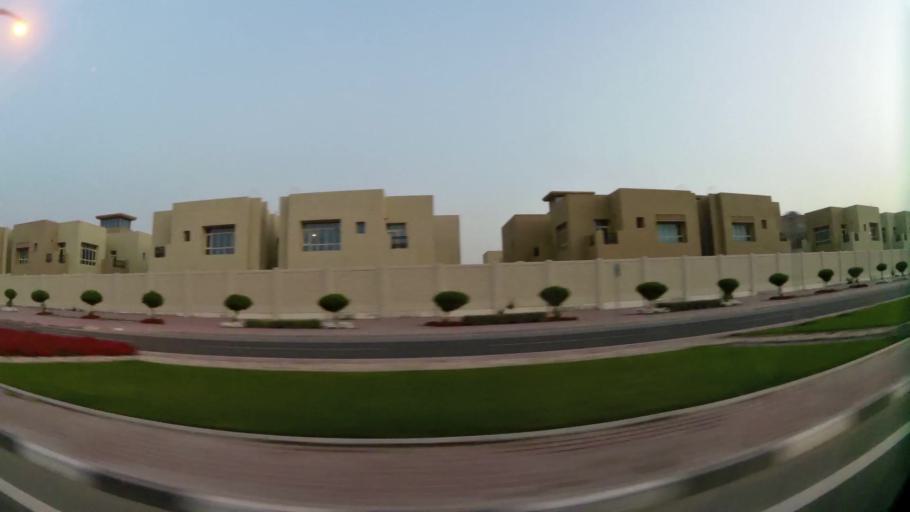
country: QA
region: Baladiyat ad Dawhah
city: Doha
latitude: 25.2655
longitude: 51.4766
